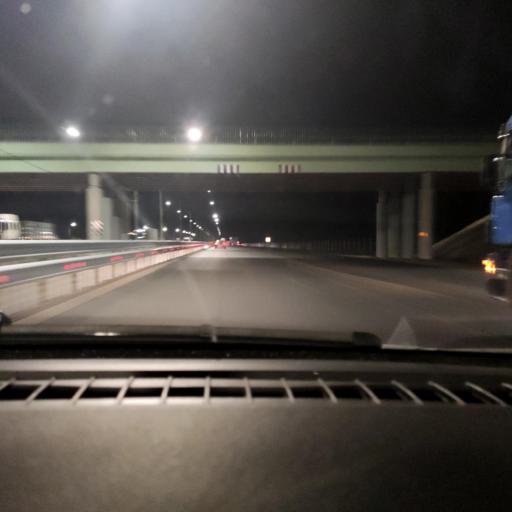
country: RU
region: Voronezj
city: Ramon'
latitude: 52.0073
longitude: 39.2128
